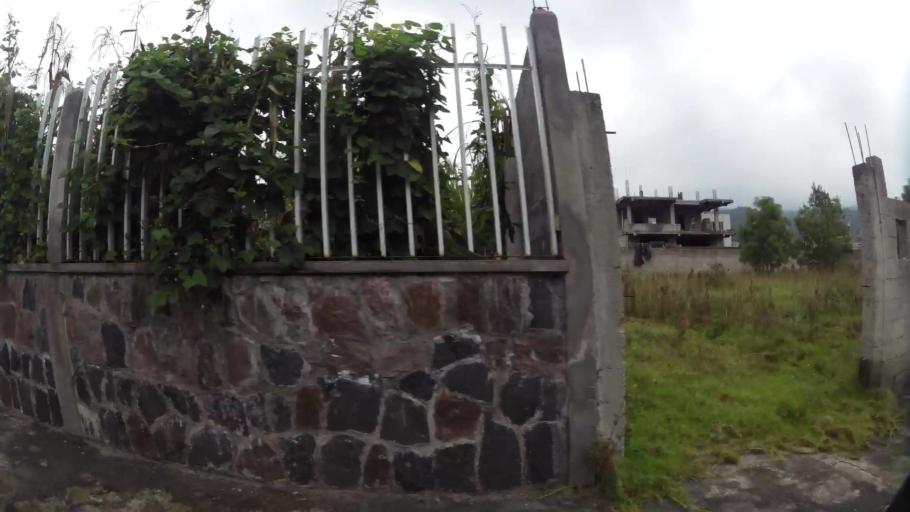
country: EC
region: Pichincha
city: Quito
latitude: -0.2694
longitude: -78.4737
